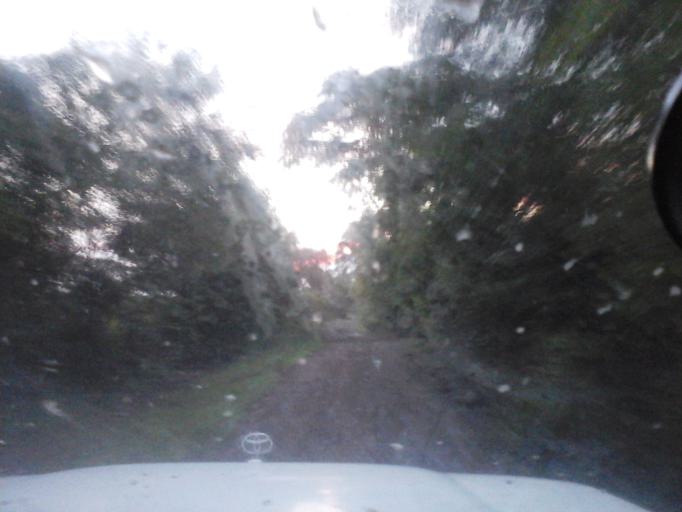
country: CO
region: Cesar
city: Agustin Codazzi
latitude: 10.1575
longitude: -73.2082
